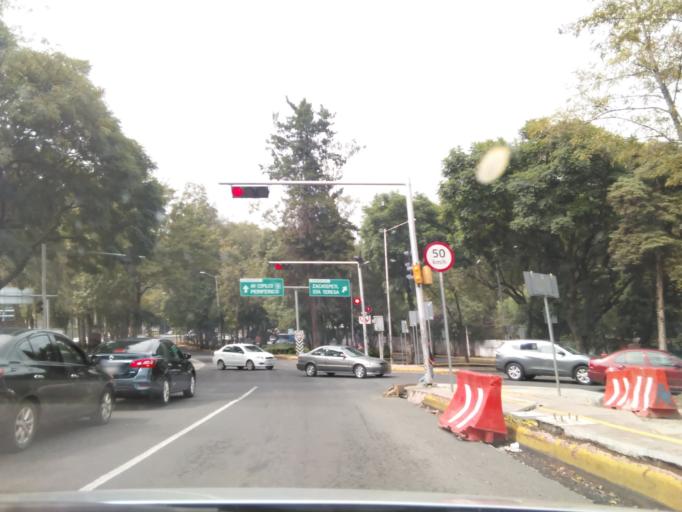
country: MX
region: Mexico City
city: Tlalpan
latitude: 19.2950
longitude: -99.1827
